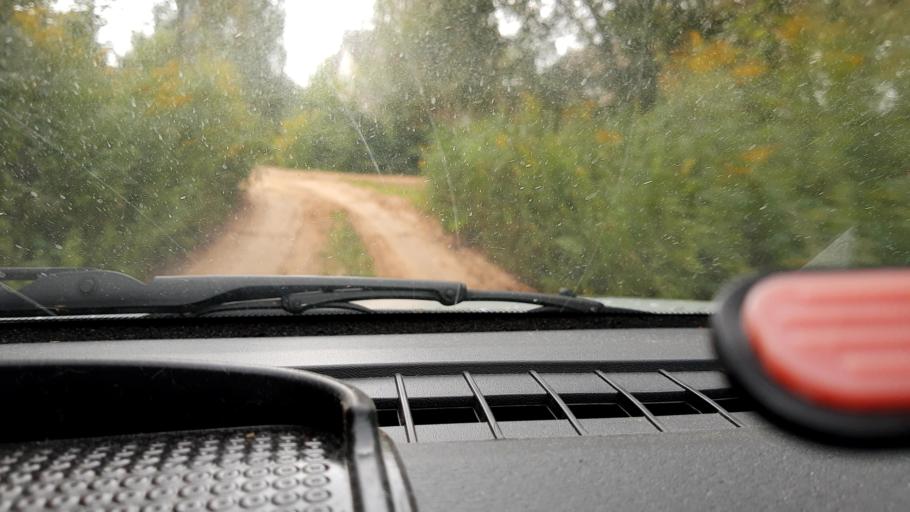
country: RU
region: Nizjnij Novgorod
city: Afonino
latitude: 56.3215
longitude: 44.1607
